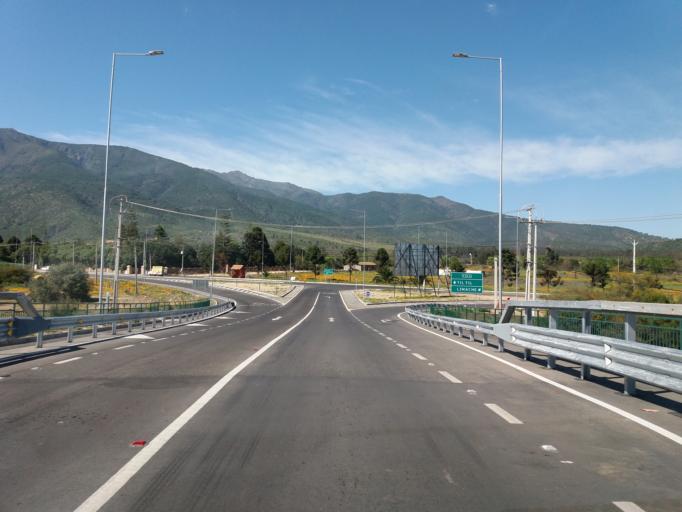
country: CL
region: Valparaiso
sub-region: Provincia de Marga Marga
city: Limache
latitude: -33.0190
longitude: -71.1714
